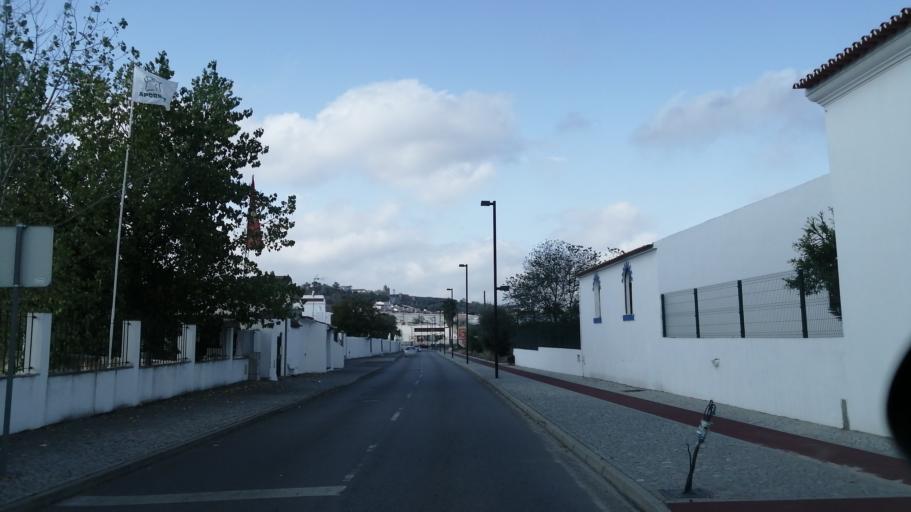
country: PT
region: Evora
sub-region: Montemor-O-Novo
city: Montemor-o-Novo
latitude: 38.6459
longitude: -8.2038
